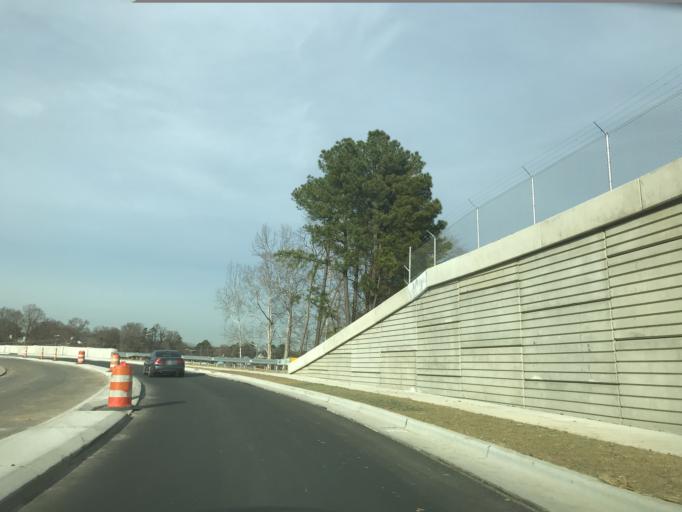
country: US
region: North Carolina
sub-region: Wake County
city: Raleigh
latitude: 35.7951
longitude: -78.6404
